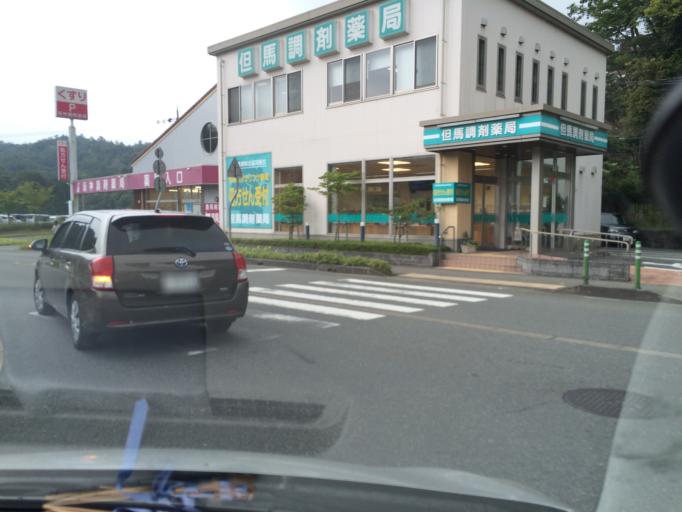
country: JP
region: Hyogo
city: Toyooka
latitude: 35.5258
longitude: 134.8060
